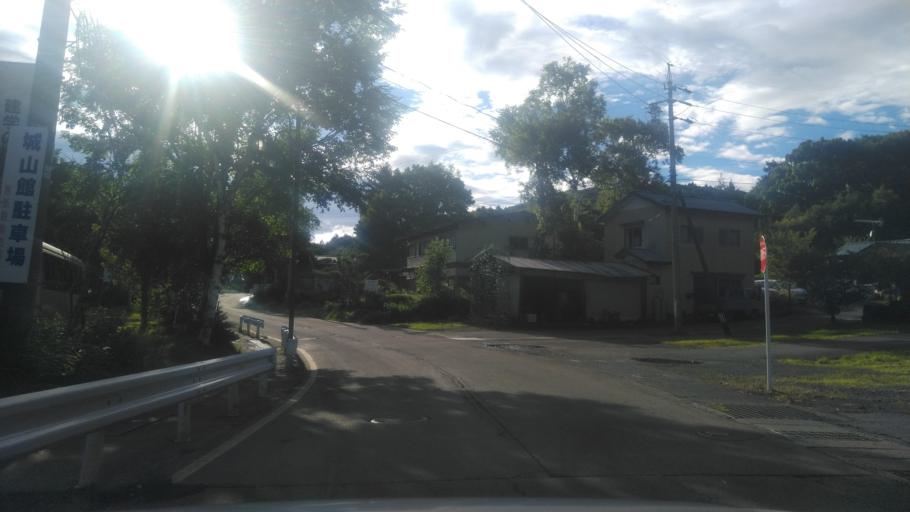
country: JP
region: Nagano
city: Suzaka
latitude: 36.5339
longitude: 138.3260
